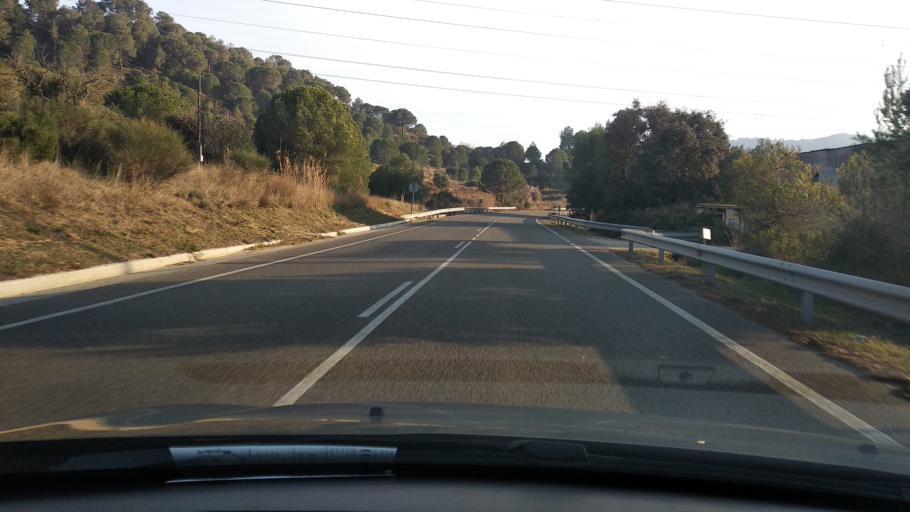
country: ES
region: Catalonia
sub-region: Provincia de Tarragona
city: Alforja
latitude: 41.1982
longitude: 0.9979
